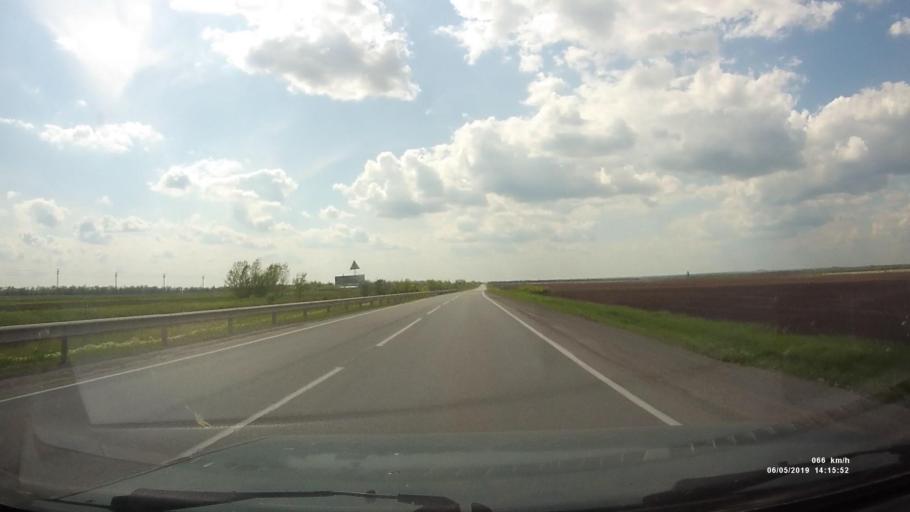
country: RU
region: Rostov
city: Kamenolomni
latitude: 47.6350
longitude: 40.2983
